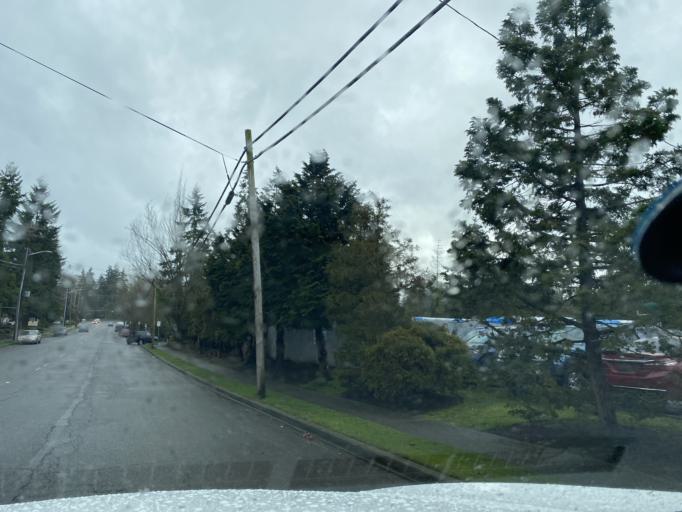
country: US
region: Washington
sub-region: Snohomish County
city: Lynnwood
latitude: 47.8204
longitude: -122.3005
